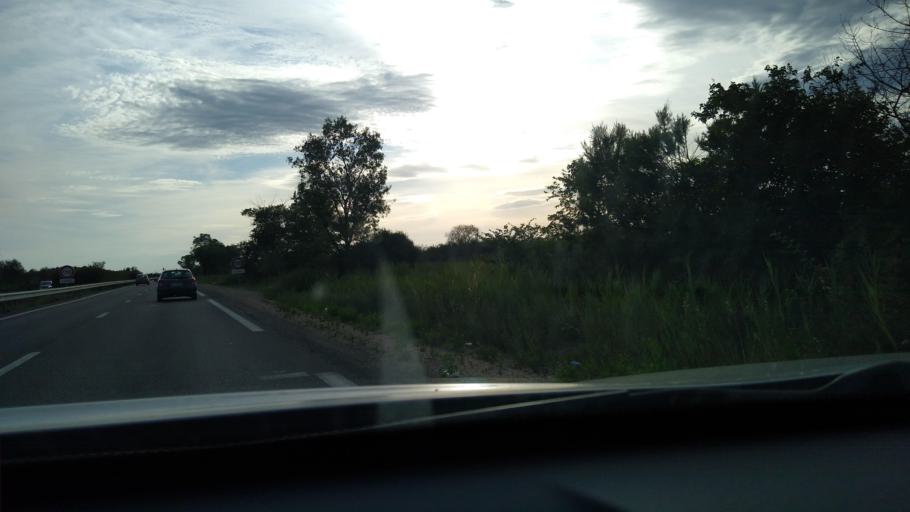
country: FR
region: Languedoc-Roussillon
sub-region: Departement de l'Herault
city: La Grande-Motte
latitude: 43.5699
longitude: 4.0744
